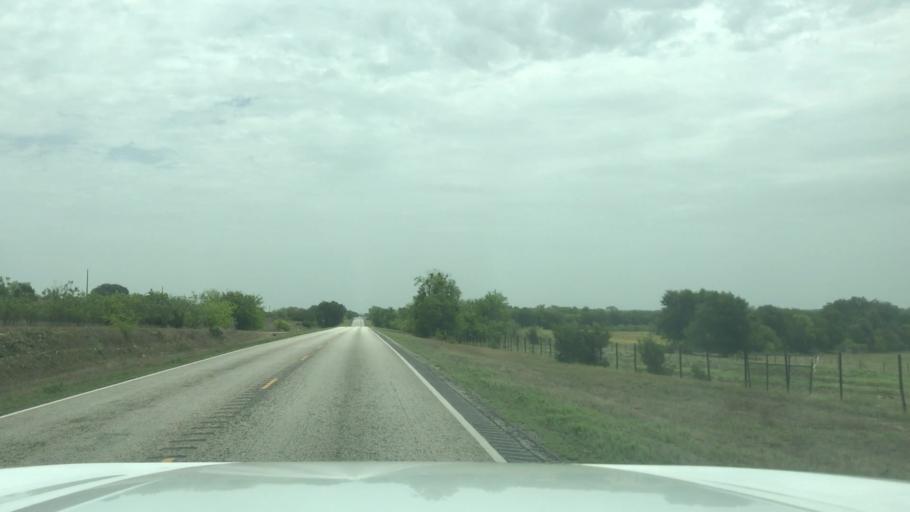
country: US
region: Texas
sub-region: Hamilton County
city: Hico
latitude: 32.0500
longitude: -98.1601
